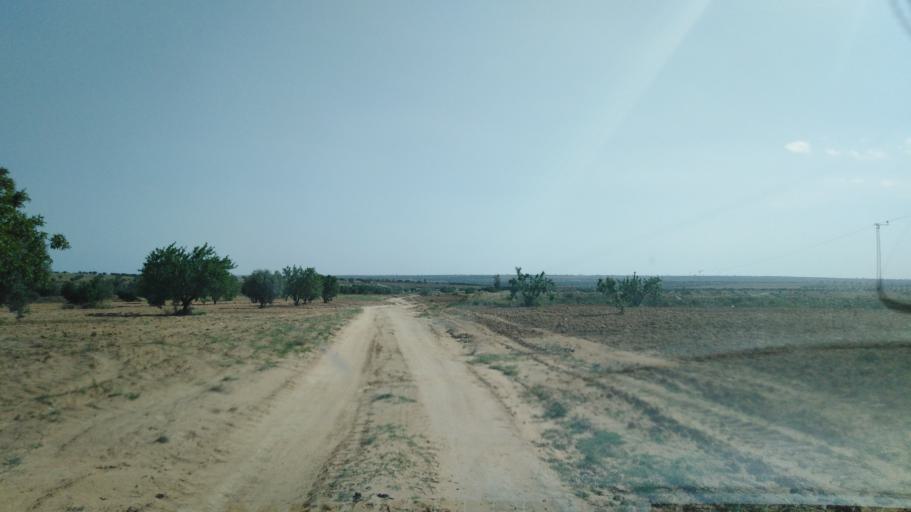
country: TN
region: Safaqis
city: Bi'r `Ali Bin Khalifah
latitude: 34.7936
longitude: 10.3722
